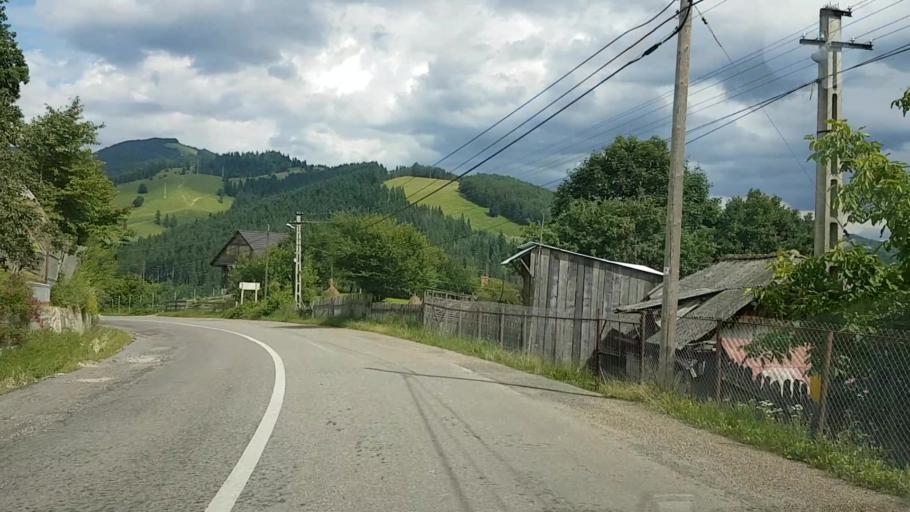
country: RO
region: Neamt
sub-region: Comuna Hangu
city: Hangu
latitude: 47.0177
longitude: 26.0738
